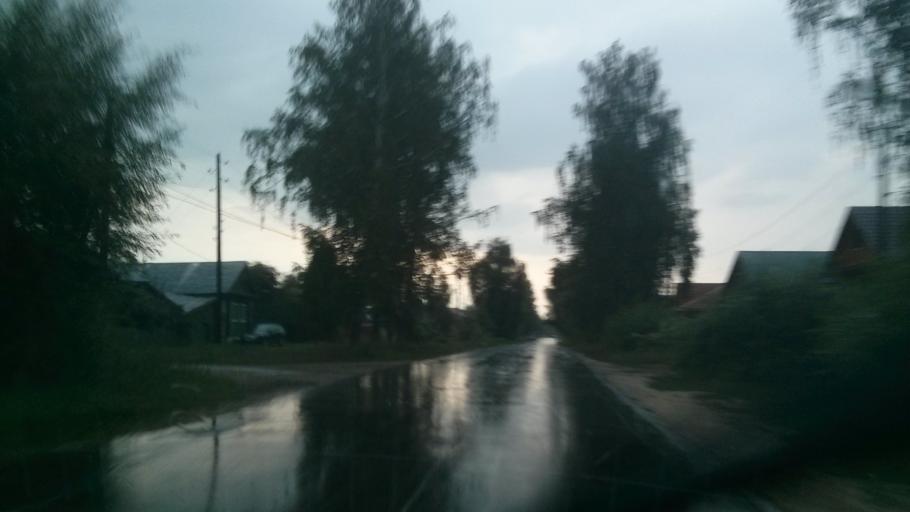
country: RU
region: Nizjnij Novgorod
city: Shimorskoye
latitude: 55.3401
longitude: 41.9288
